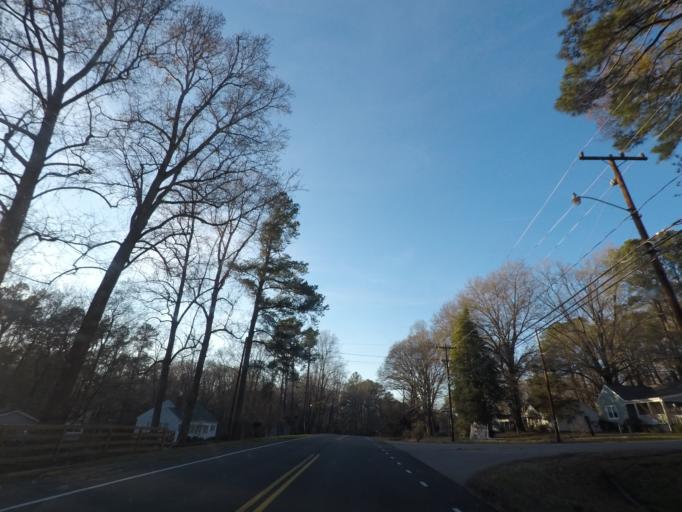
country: US
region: North Carolina
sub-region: Durham County
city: Durham
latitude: 36.0451
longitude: -78.9661
